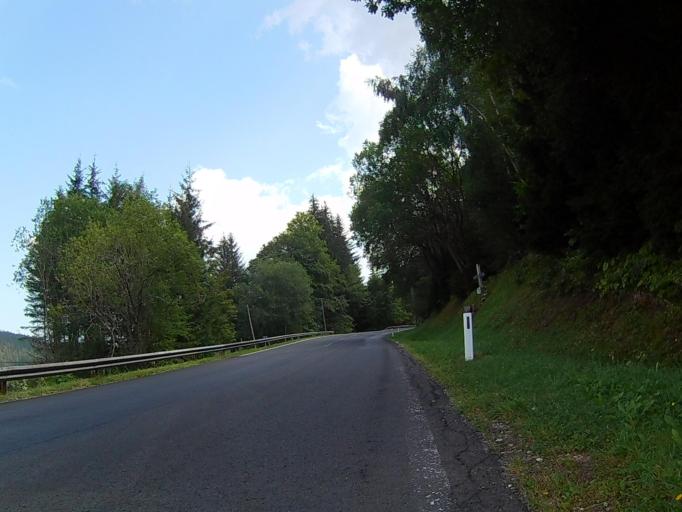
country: AT
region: Styria
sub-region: Politischer Bezirk Deutschlandsberg
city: Soboth
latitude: 46.7043
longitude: 15.0923
